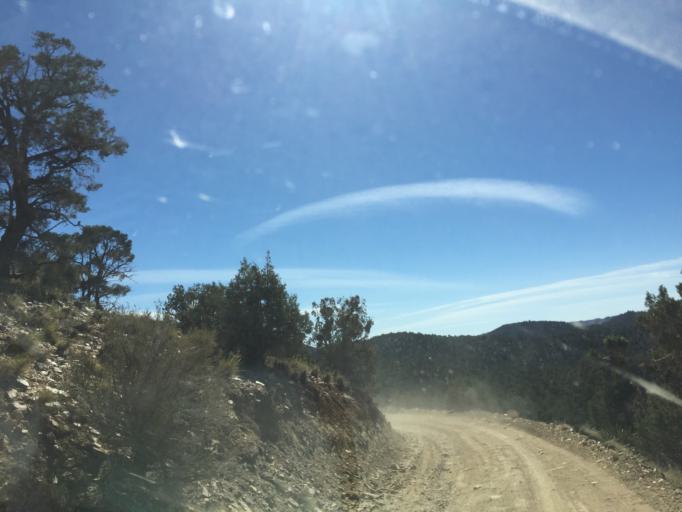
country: US
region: California
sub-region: San Bernardino County
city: Big Bear City
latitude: 34.2483
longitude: -116.7138
